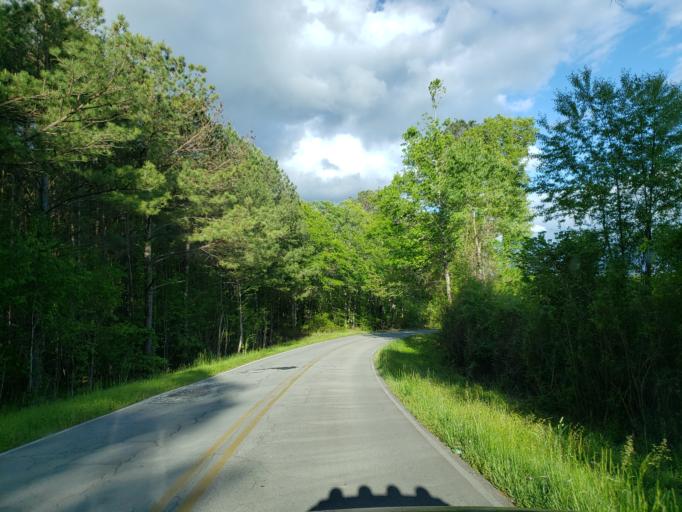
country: US
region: Georgia
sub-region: Haralson County
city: Tallapoosa
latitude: 33.7799
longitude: -85.3148
